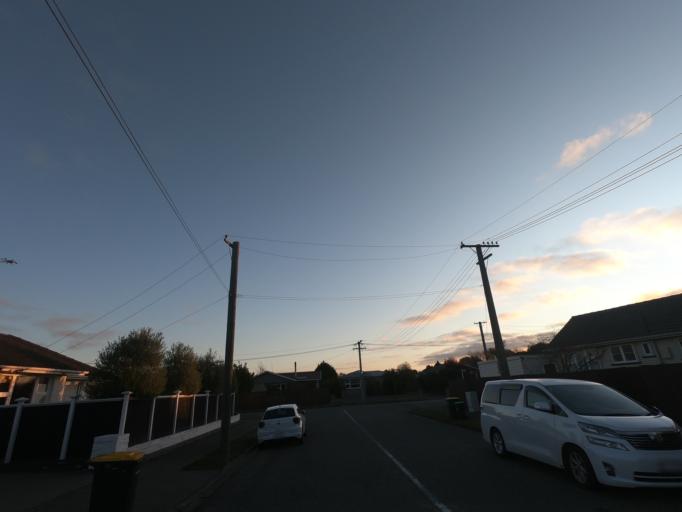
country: NZ
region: Canterbury
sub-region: Selwyn District
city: Prebbleton
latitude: -43.5761
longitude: 172.5601
